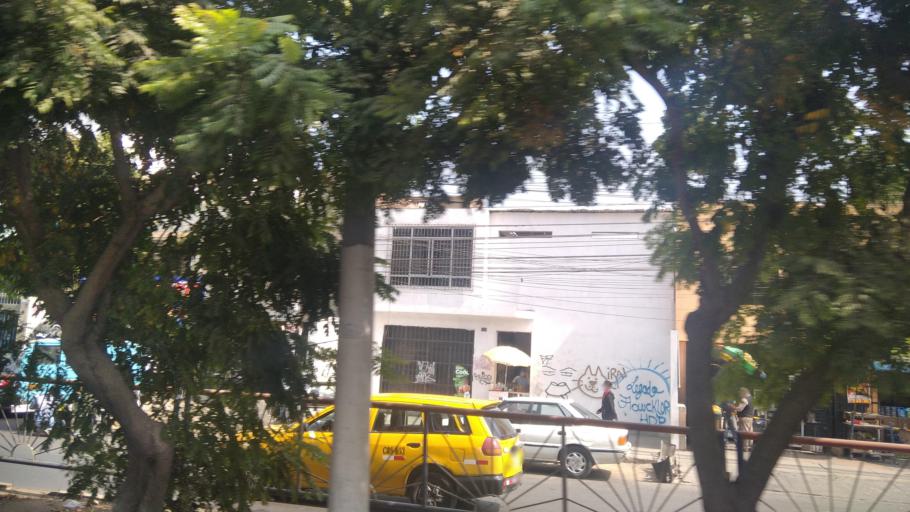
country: PE
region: Lima
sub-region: Lima
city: Independencia
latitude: -12.0042
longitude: -77.0073
